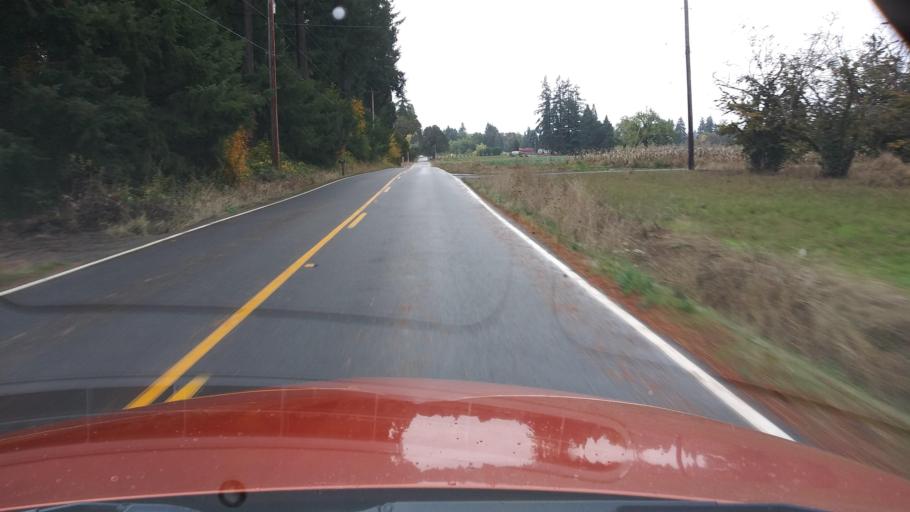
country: US
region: Oregon
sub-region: Washington County
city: Forest Grove
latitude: 45.5372
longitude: -123.0871
